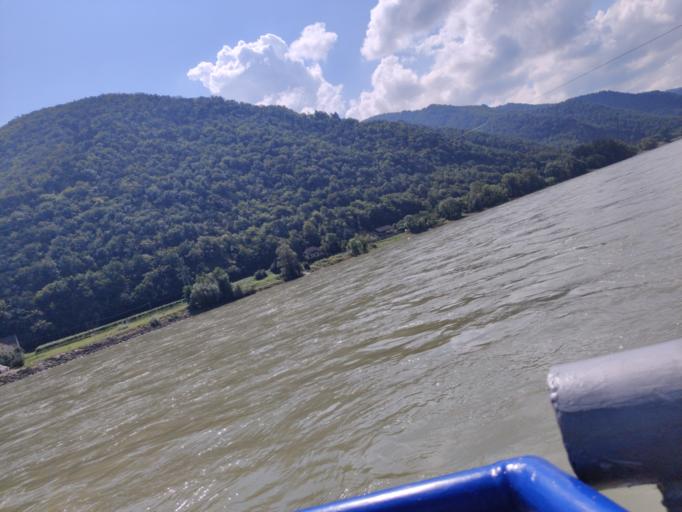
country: AT
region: Lower Austria
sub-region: Politischer Bezirk Krems
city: Durnstein
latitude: 48.3945
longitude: 15.4729
